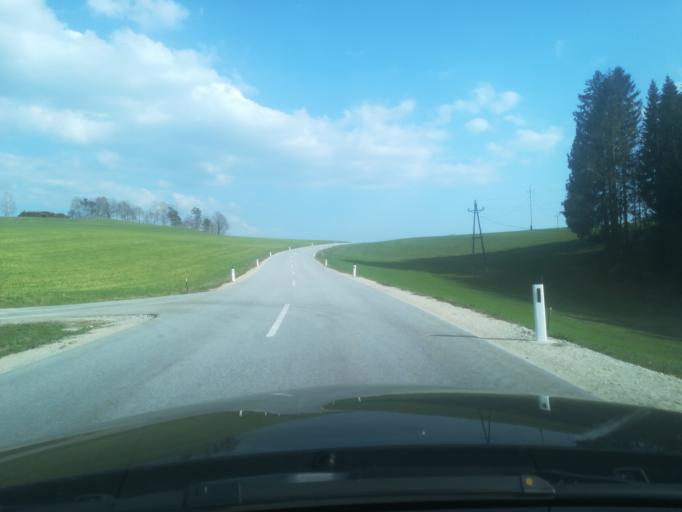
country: AT
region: Upper Austria
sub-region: Politischer Bezirk Perg
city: Perg
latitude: 48.3604
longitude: 14.6583
